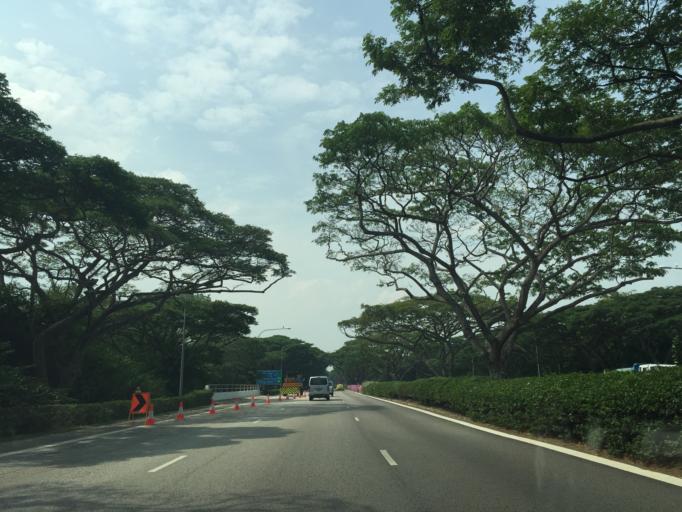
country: SG
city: Singapore
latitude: 1.3299
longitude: 103.9753
